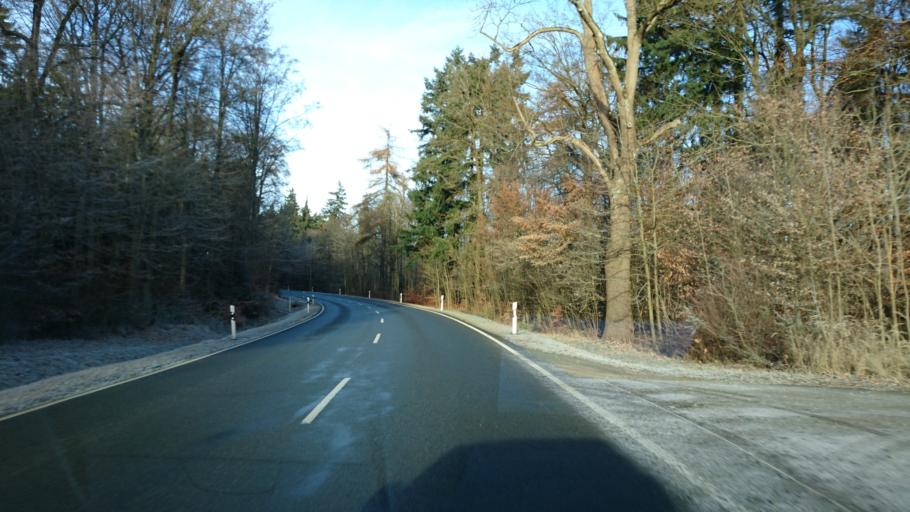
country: DE
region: Thuringia
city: Tanna
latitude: 50.5443
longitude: 11.8587
